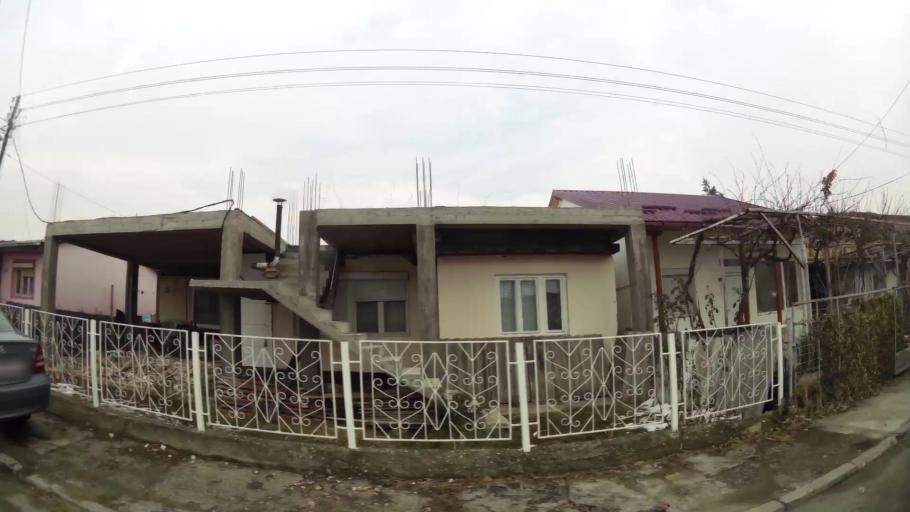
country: MK
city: Creshevo
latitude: 42.0010
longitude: 21.4923
